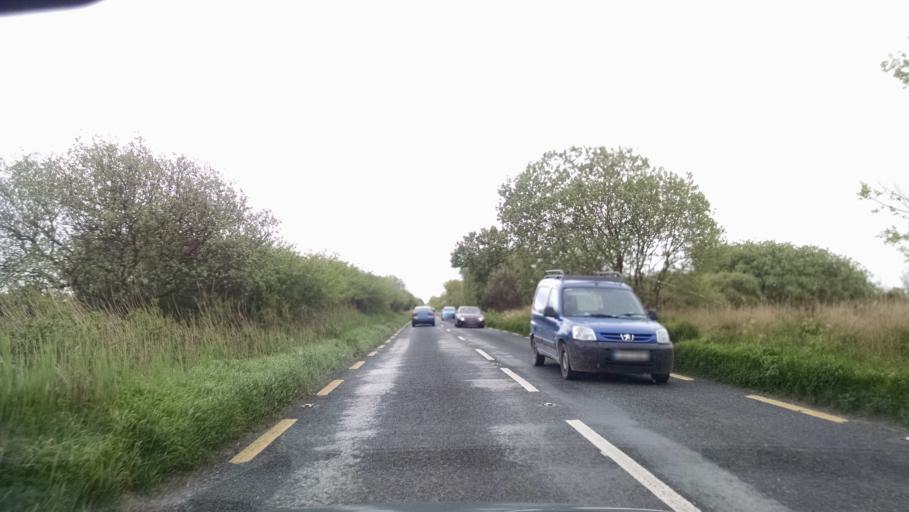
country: IE
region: Connaught
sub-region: County Galway
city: Claregalway
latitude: 53.3968
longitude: -9.0174
